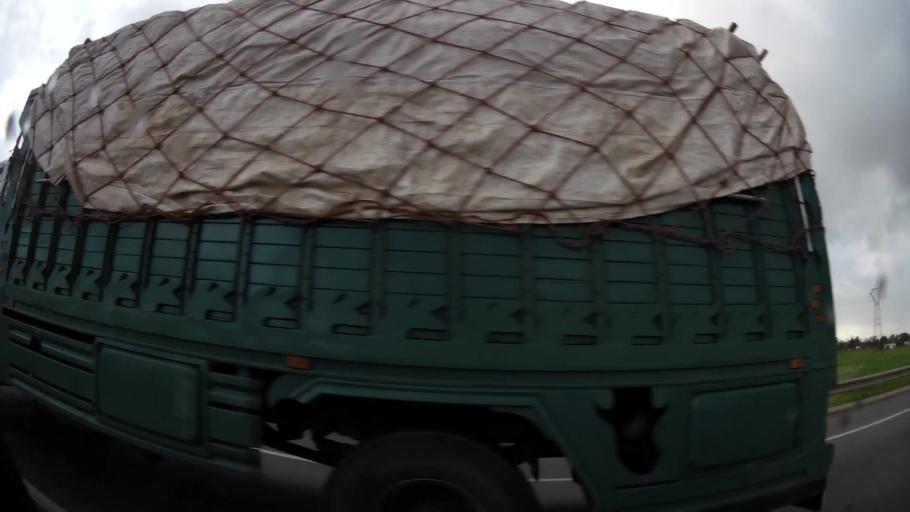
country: MA
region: Grand Casablanca
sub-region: Mohammedia
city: Mohammedia
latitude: 33.6399
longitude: -7.4217
